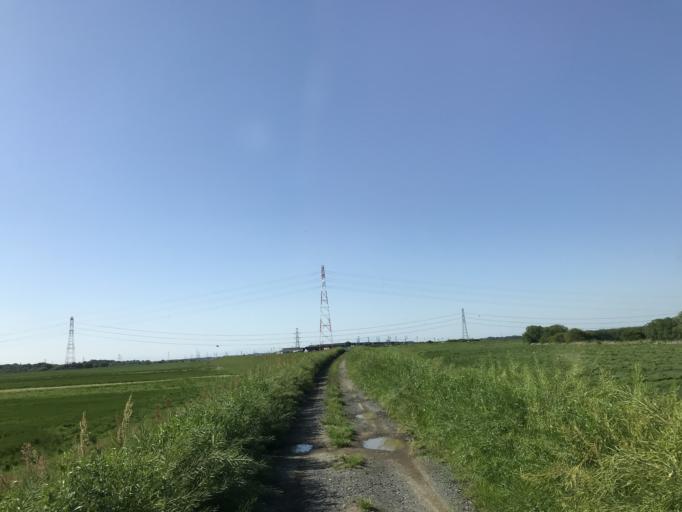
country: JP
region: Ibaraki
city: Moriya
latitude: 35.9423
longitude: 139.9441
